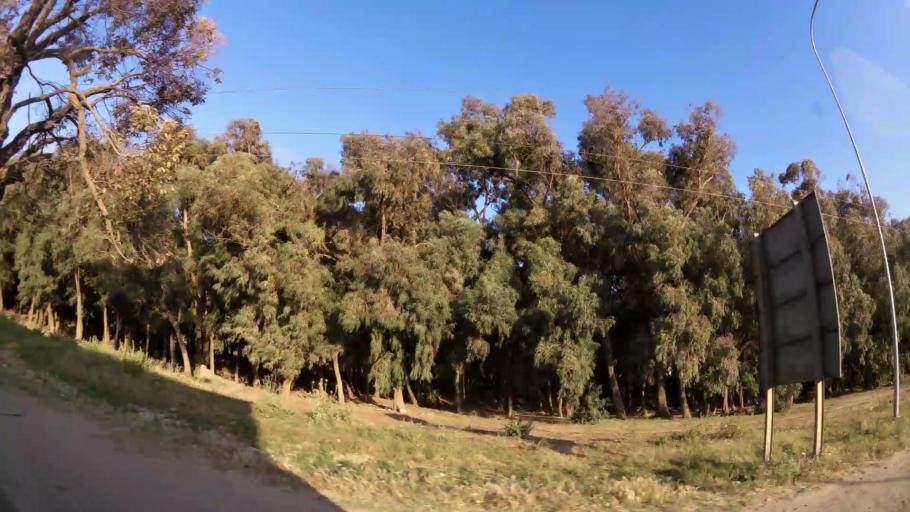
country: MA
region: Rabat-Sale-Zemmour-Zaer
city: Sale
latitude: 34.1075
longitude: -6.7536
